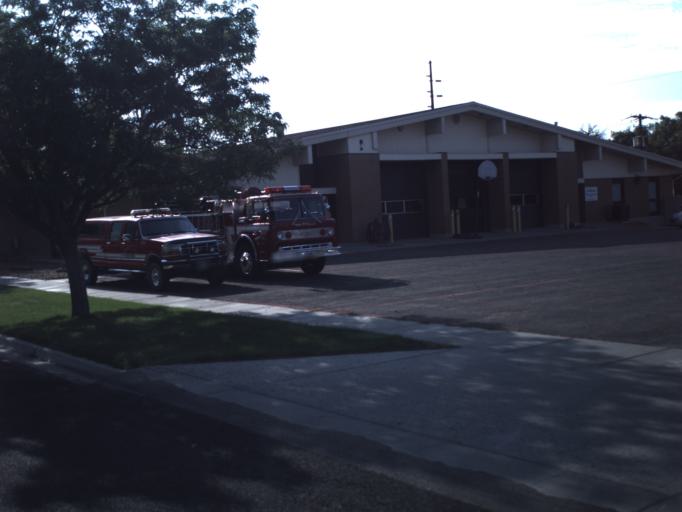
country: US
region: Utah
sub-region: Carbon County
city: Price
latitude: 39.6010
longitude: -110.8081
